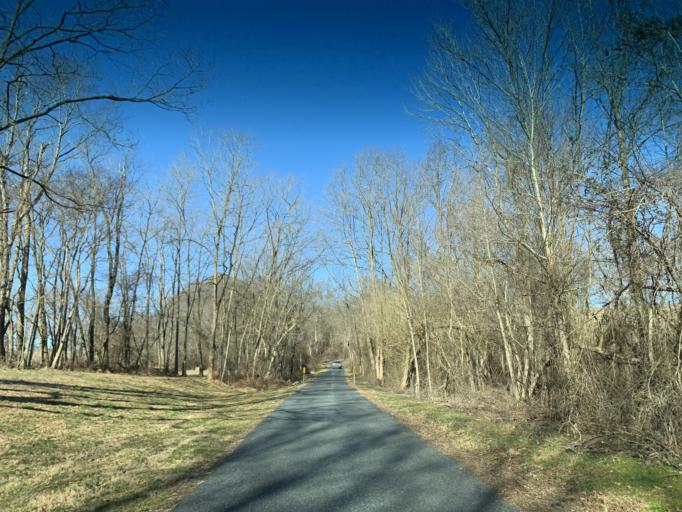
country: US
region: Maryland
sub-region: Harford County
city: South Bel Air
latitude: 39.6186
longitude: -76.2431
